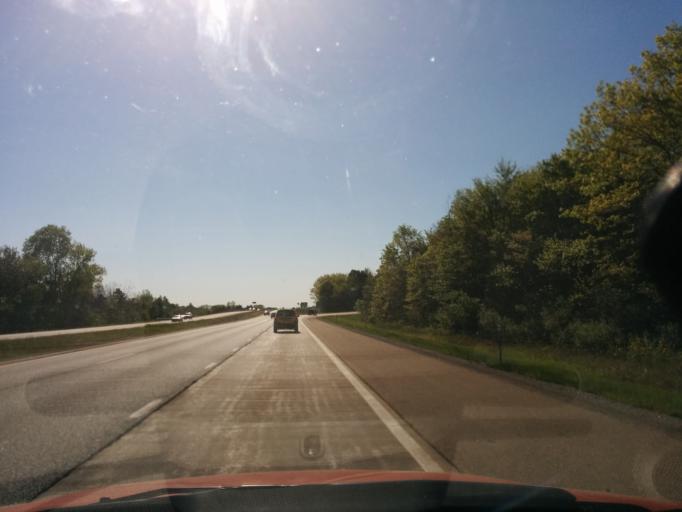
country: US
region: Michigan
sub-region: Midland County
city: Midland
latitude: 43.6561
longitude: -84.2409
